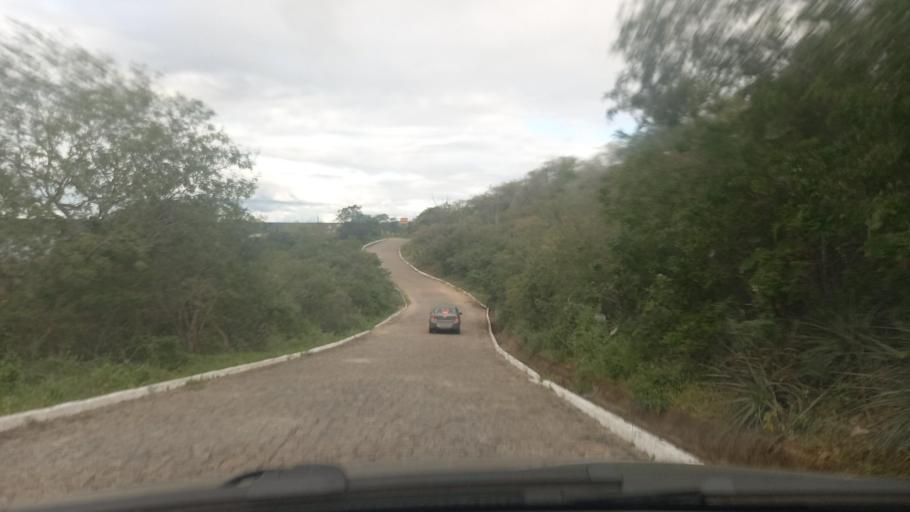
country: BR
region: Sergipe
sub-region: Caninde De Sao Francisco
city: Caninde de Sao Francisco
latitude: -9.6184
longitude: -37.8052
